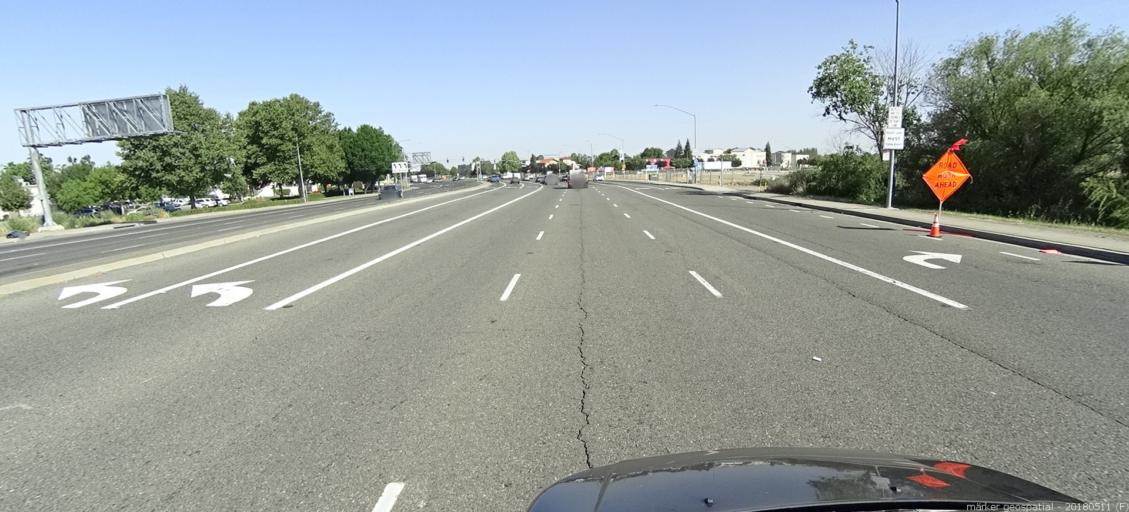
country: US
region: California
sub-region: Sacramento County
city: Sacramento
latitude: 38.6362
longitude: -121.5024
